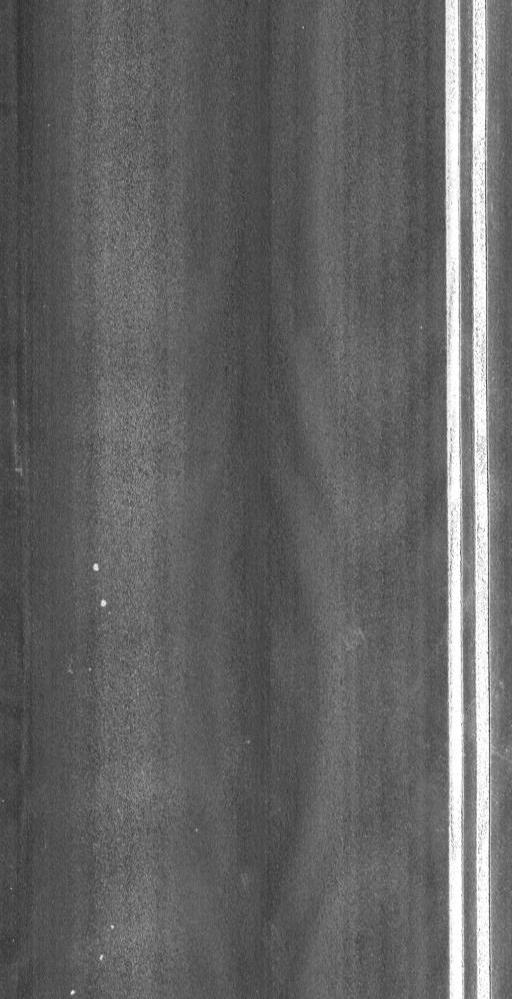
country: US
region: Vermont
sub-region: Chittenden County
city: Burlington
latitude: 44.3712
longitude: -73.2248
